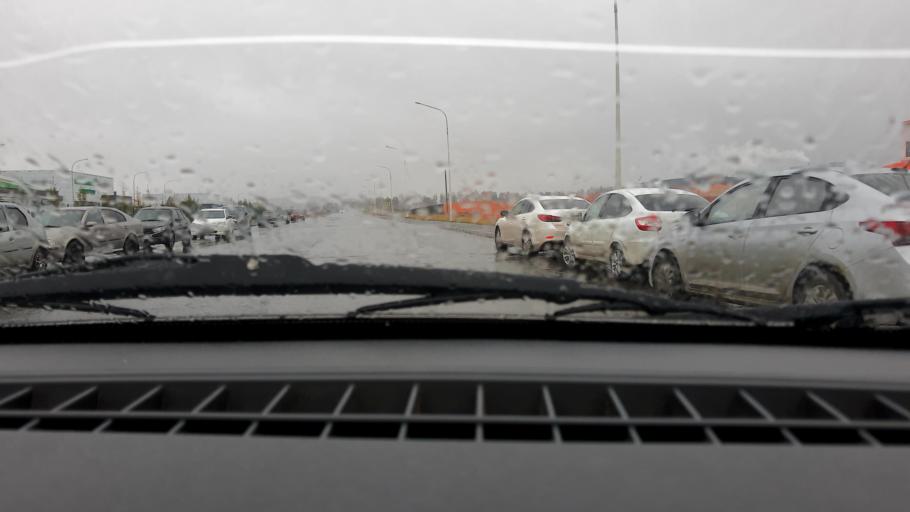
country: RU
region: Bashkortostan
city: Ufa
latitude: 54.6033
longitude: 55.9050
